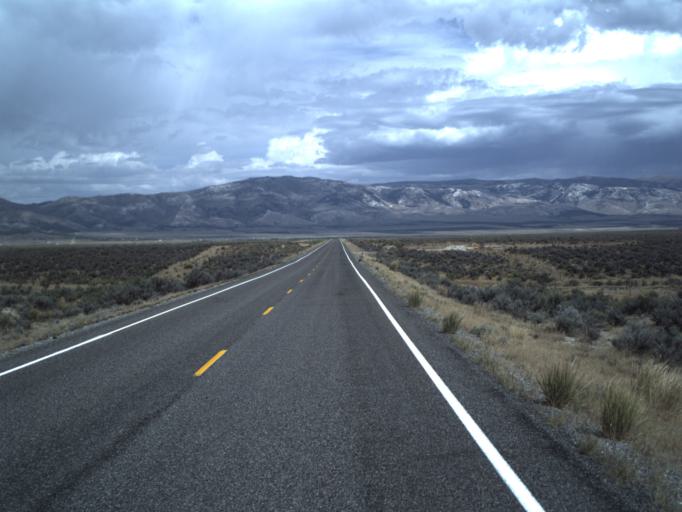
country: US
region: Idaho
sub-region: Cassia County
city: Burley
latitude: 41.7358
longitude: -113.5211
